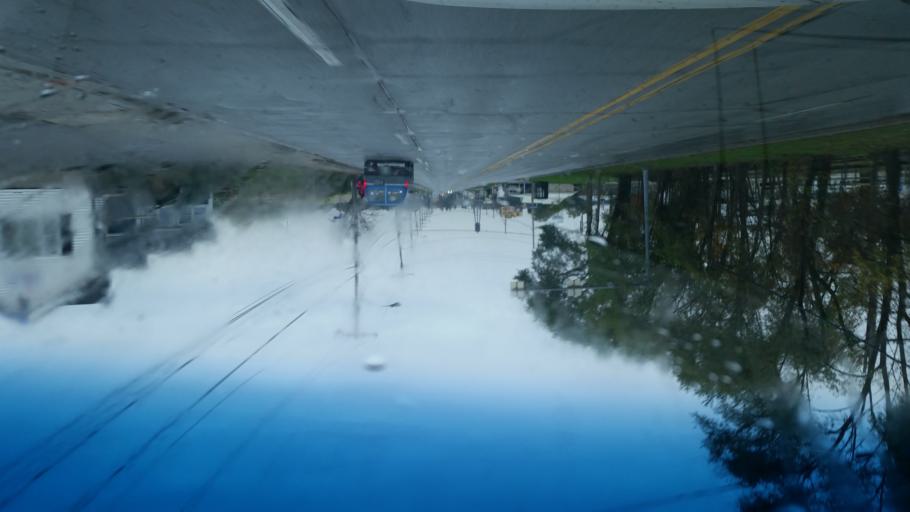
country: US
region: Indiana
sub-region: Howard County
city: Kokomo
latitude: 40.4665
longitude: -86.1242
